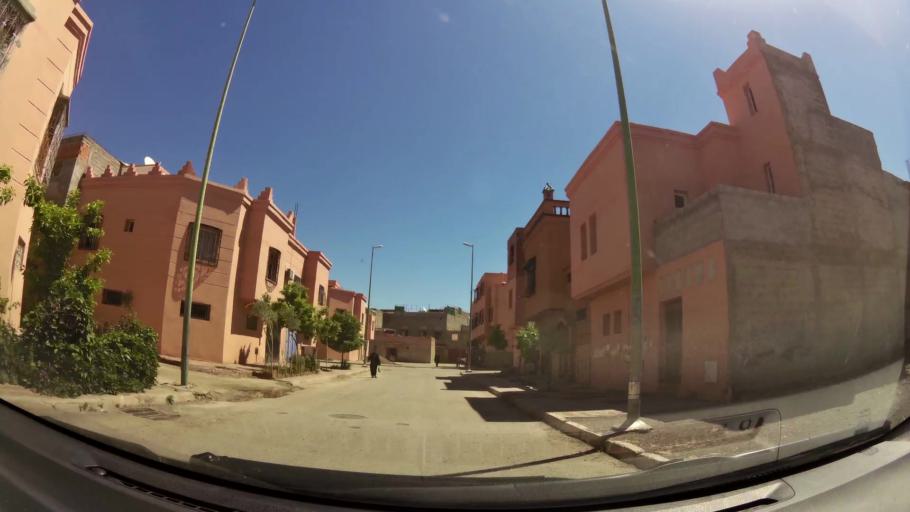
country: MA
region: Marrakech-Tensift-Al Haouz
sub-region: Marrakech
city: Marrakesh
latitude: 31.5734
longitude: -7.9833
